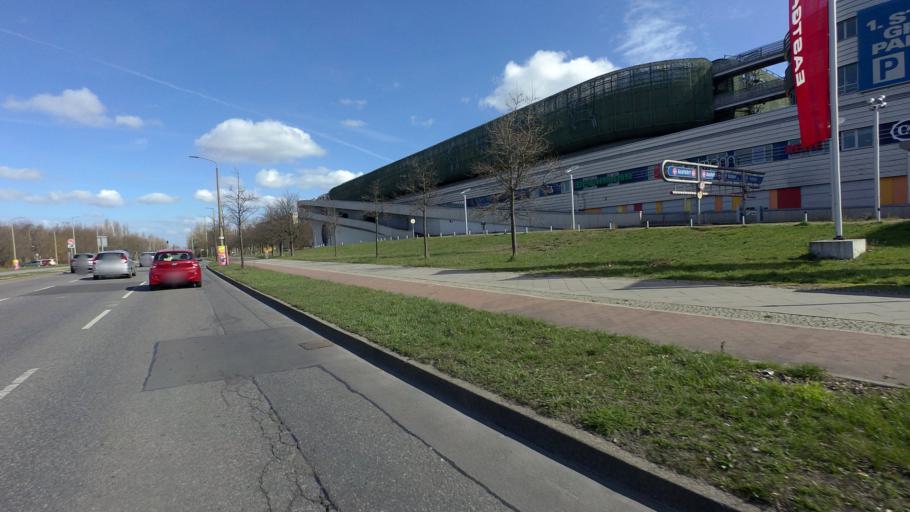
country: DE
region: Berlin
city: Falkenberg
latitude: 52.5438
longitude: 13.5426
